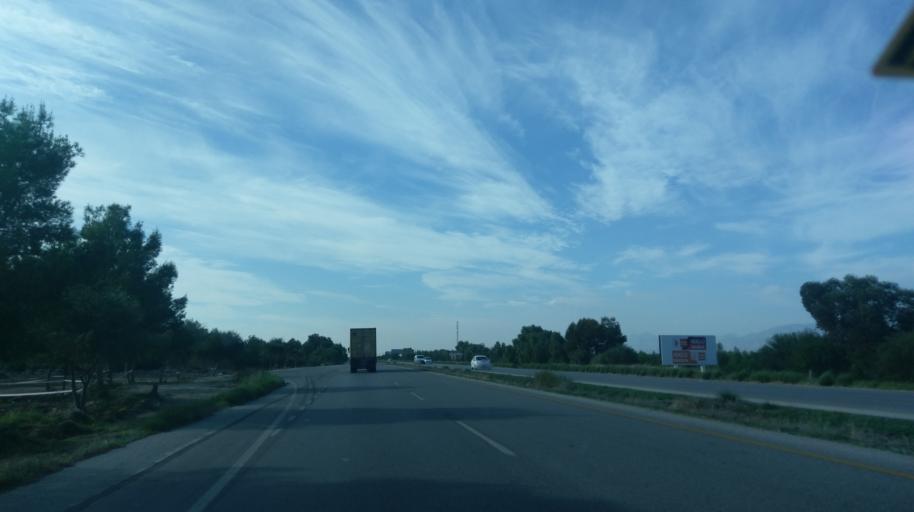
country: CY
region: Ammochostos
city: Lefkonoiko
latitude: 35.1857
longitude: 33.6601
